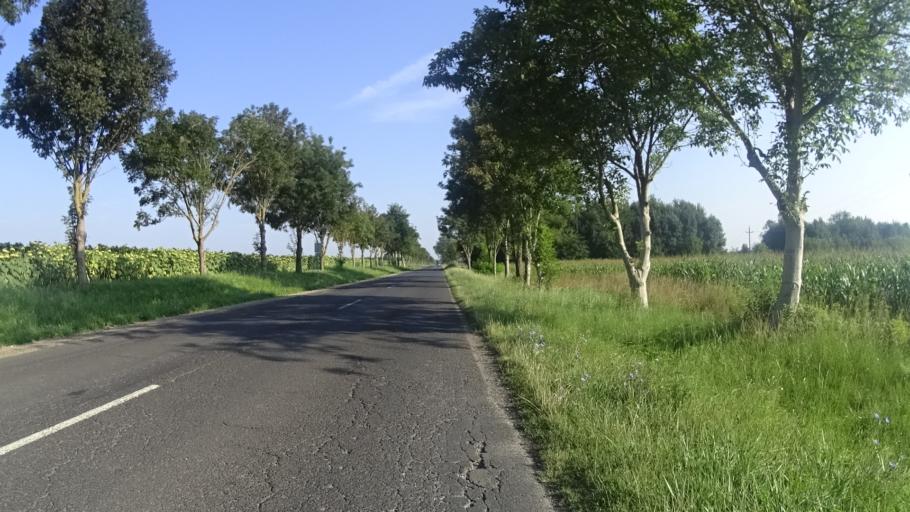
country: HU
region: Zala
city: Sarmellek
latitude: 46.6736
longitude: 17.1731
